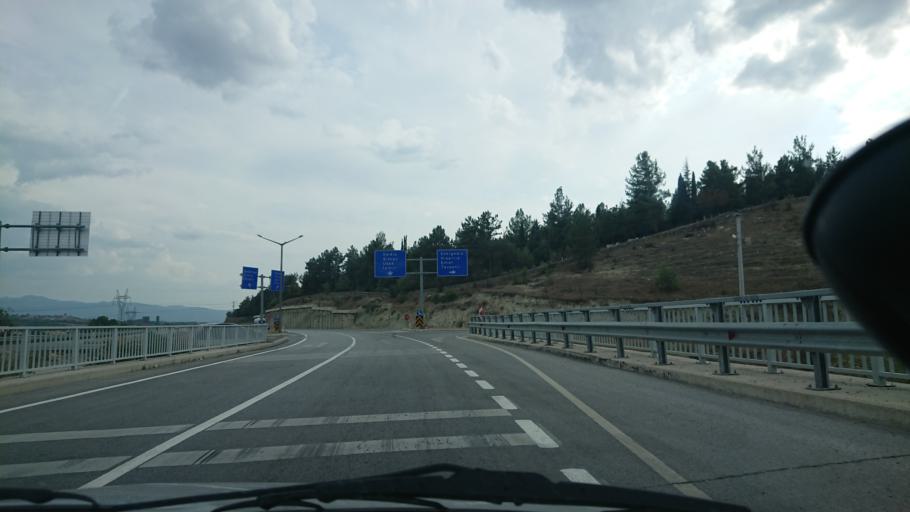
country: TR
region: Kuetahya
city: Gediz
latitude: 39.0319
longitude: 29.4163
